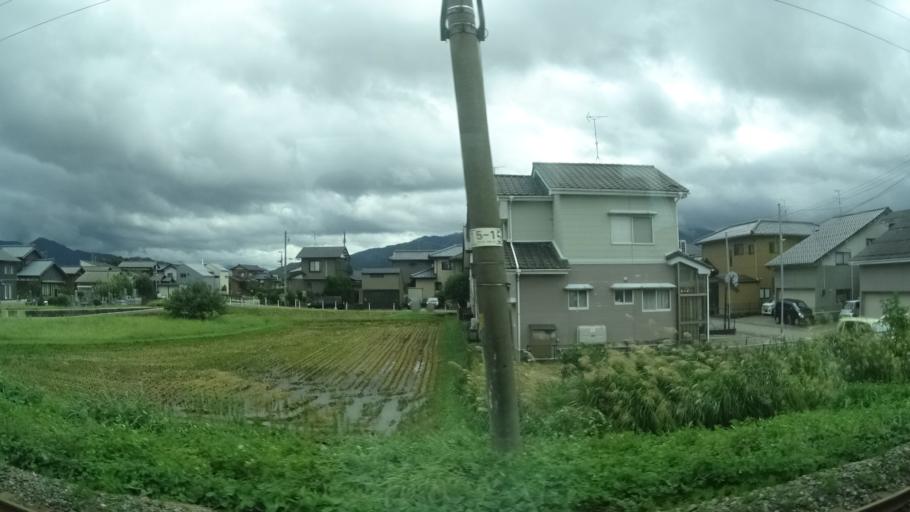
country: JP
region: Niigata
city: Murakami
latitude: 38.1156
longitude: 139.4428
